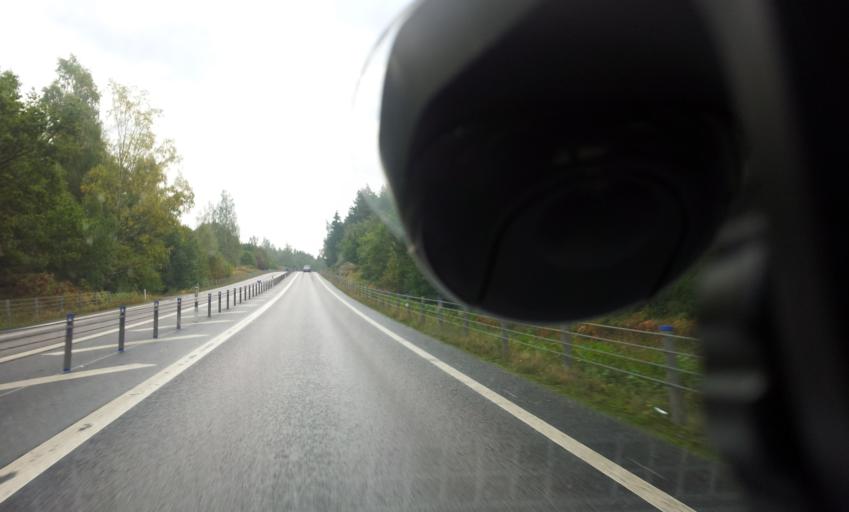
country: SE
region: Kalmar
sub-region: Vasterviks Kommun
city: Gamleby
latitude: 57.8654
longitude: 16.4199
